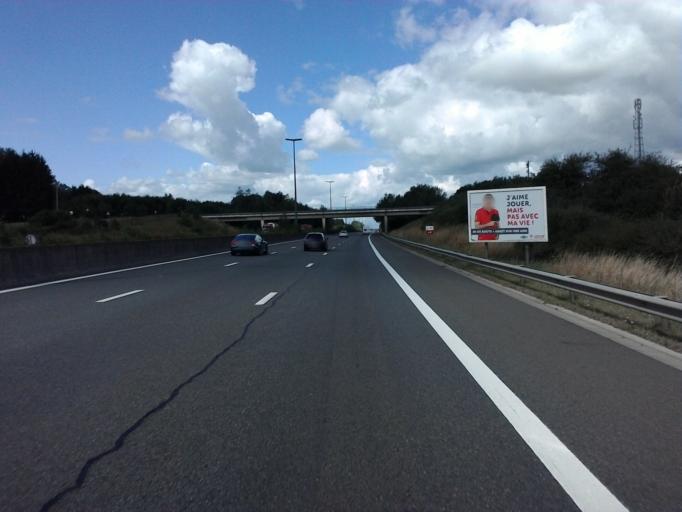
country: BE
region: Wallonia
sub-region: Province du Luxembourg
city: Habay-la-Vieille
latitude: 49.6966
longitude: 5.6657
